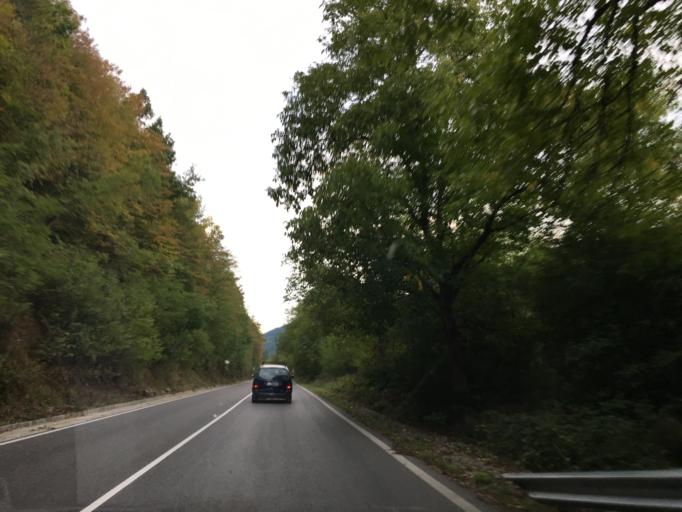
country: BG
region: Sofiya
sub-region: Obshtina Svoge
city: Svoge
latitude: 42.9423
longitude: 23.3843
